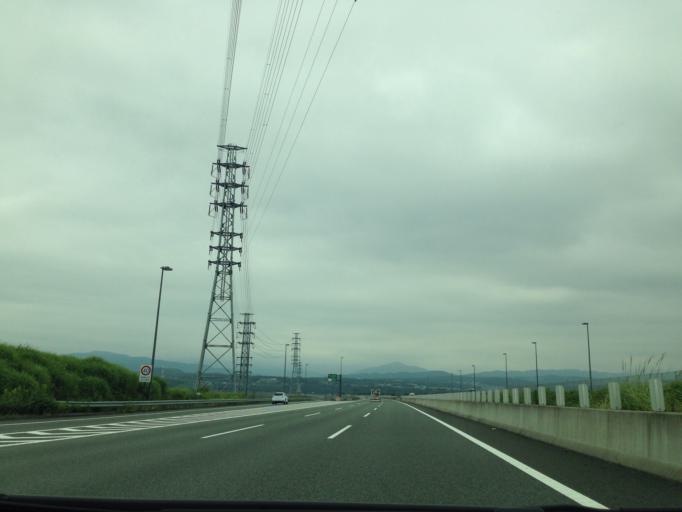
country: JP
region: Shizuoka
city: Fuji
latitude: 35.2025
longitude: 138.6699
